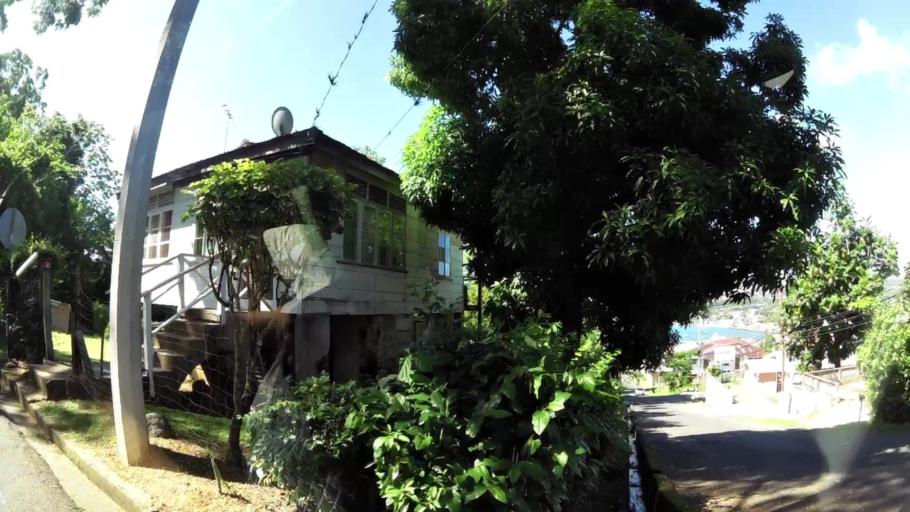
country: TT
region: Tobago
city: Scarborough
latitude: 11.1816
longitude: -60.7312
